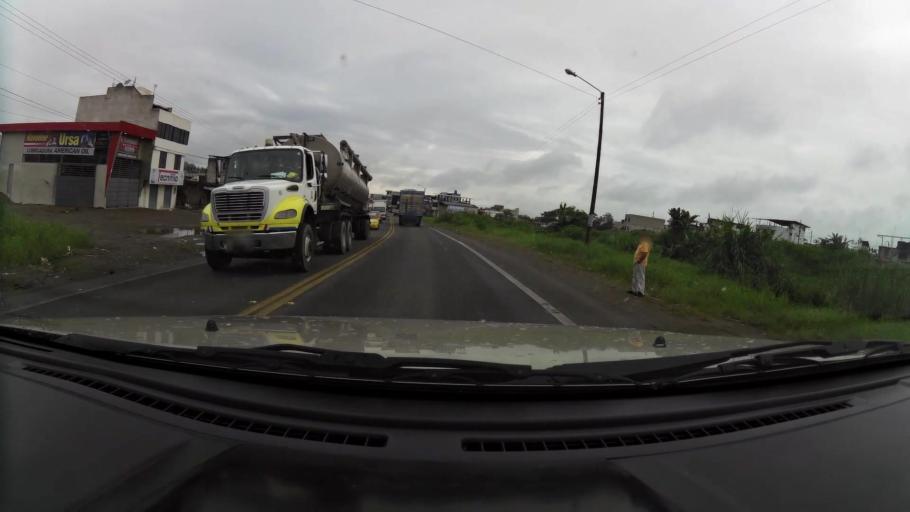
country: EC
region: Santo Domingo de los Tsachilas
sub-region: Canton Santo Domingo de los Colorados
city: Santo Domingo de los Colorados
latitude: -0.2372
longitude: -79.1790
